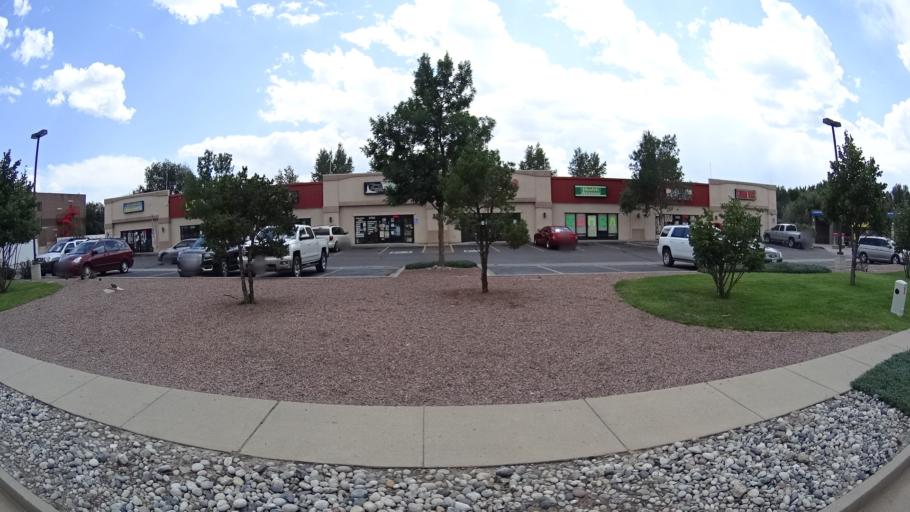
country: US
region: Colorado
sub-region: El Paso County
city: Stratmoor
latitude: 38.8319
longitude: -104.7595
